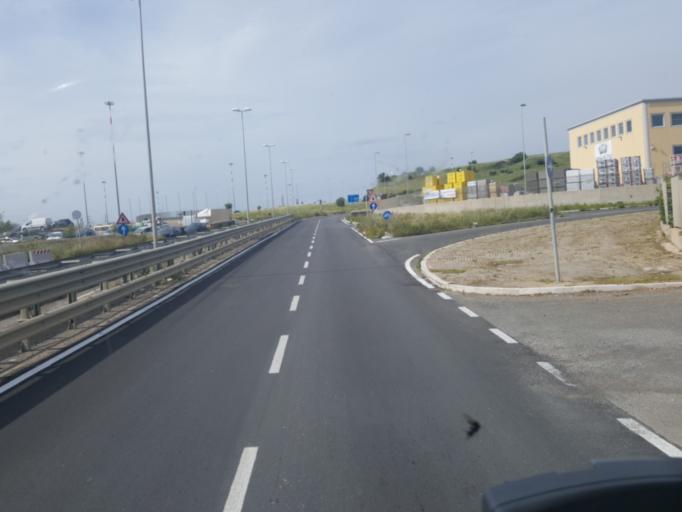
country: IT
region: Latium
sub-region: Citta metropolitana di Roma Capitale
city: Aurelia
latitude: 42.1229
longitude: 11.7782
